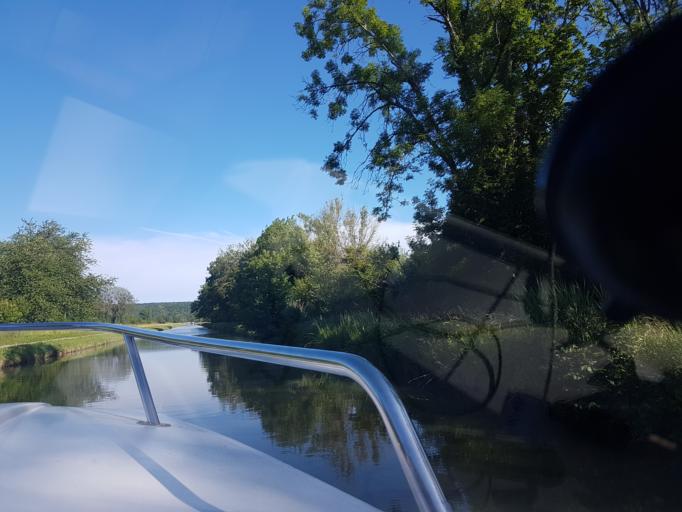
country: FR
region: Bourgogne
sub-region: Departement de la Nievre
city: Clamecy
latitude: 47.5311
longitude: 3.6170
